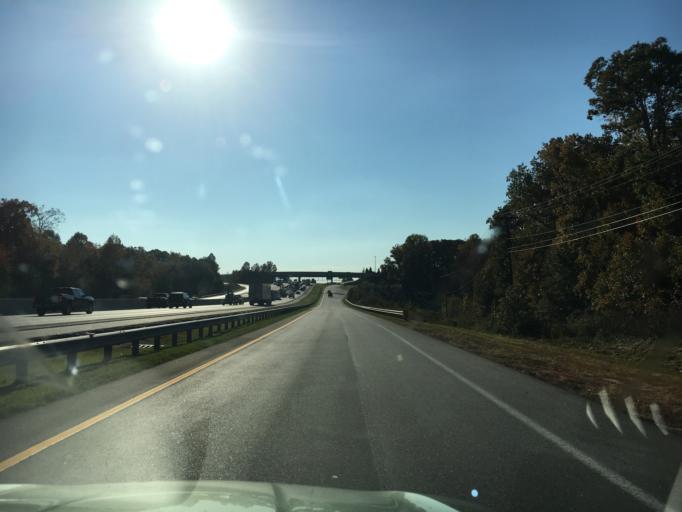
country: US
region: South Carolina
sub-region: Greenville County
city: Greer
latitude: 34.8795
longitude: -82.2081
